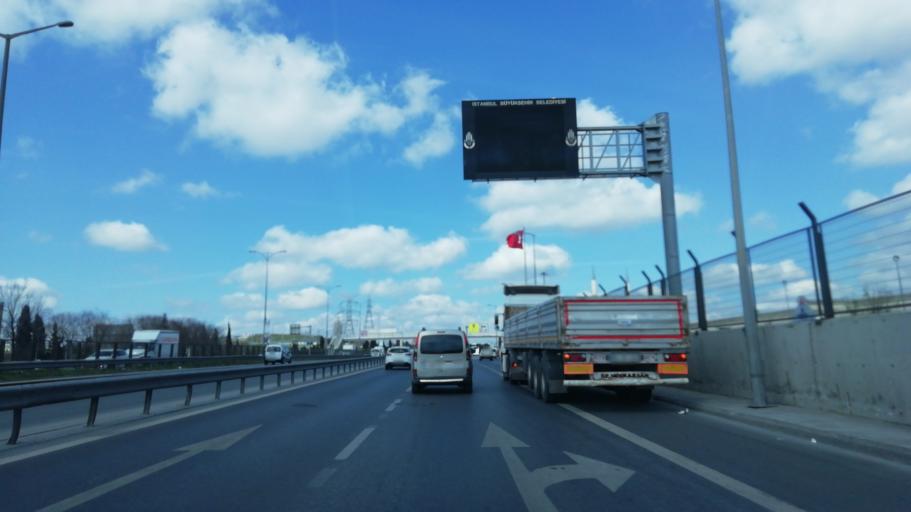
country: TR
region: Istanbul
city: Esenler
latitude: 41.0474
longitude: 28.8851
